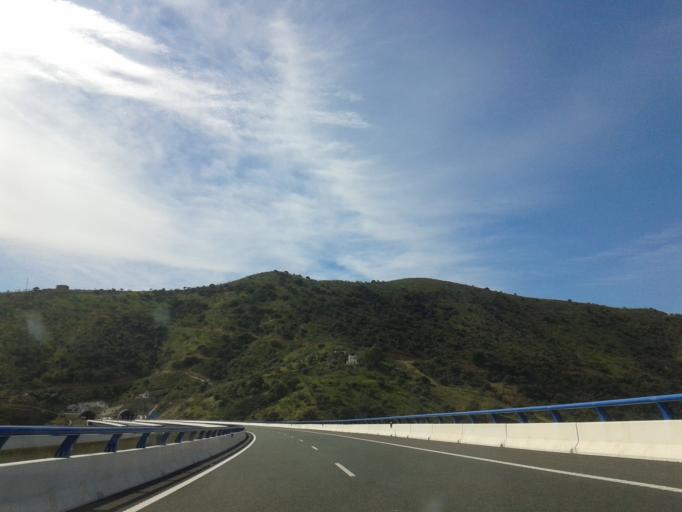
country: ES
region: Andalusia
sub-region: Provincia de Malaga
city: Casabermeja
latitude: 36.8760
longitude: -4.4819
